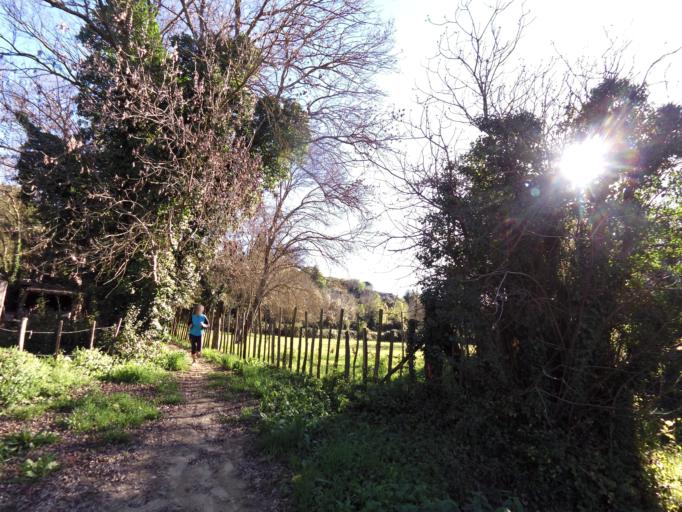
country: FR
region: Languedoc-Roussillon
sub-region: Departement du Gard
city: Aubais
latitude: 43.7572
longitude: 4.1440
